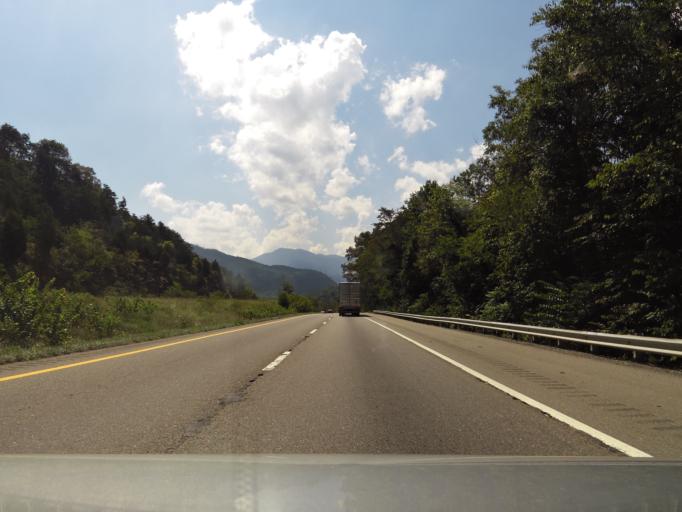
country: US
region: Tennessee
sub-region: Cocke County
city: Newport
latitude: 35.8504
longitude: -83.1835
